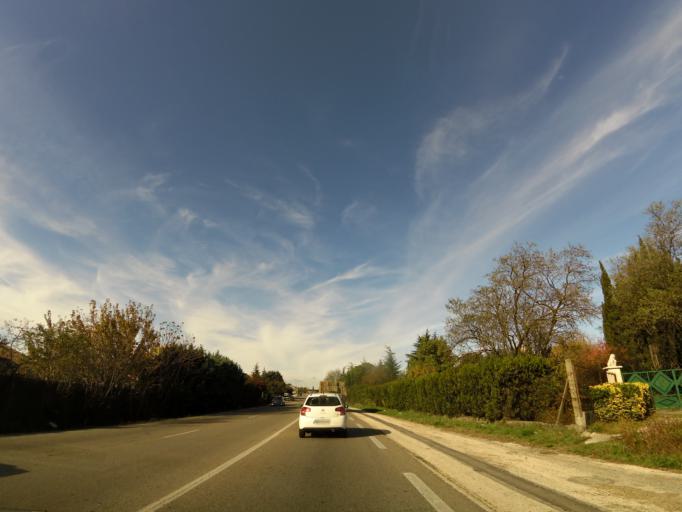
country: FR
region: Languedoc-Roussillon
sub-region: Departement du Gard
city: Ales
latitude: 44.1226
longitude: 4.1088
